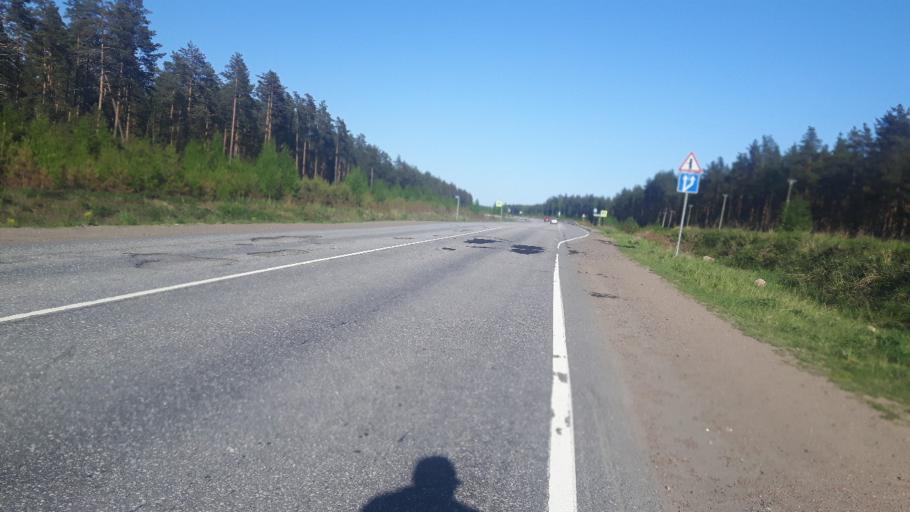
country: RU
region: Leningrad
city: Lebyazh'ye
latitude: 60.1686
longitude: 29.2149
